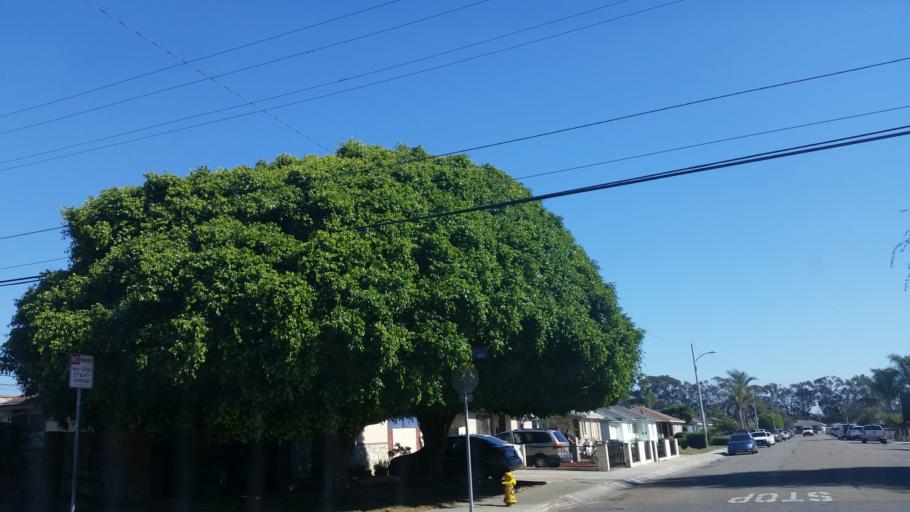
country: US
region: California
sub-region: Ventura County
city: Oxnard
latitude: 34.1773
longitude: -119.1723
